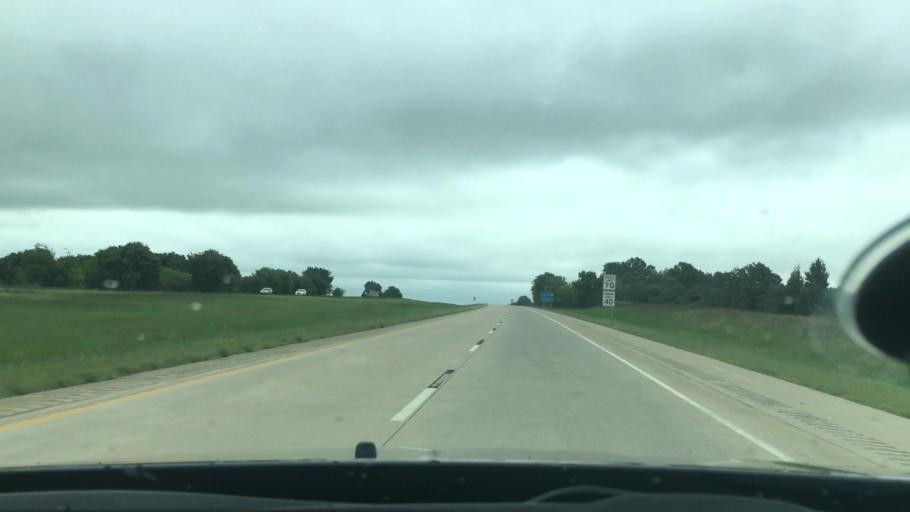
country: US
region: Oklahoma
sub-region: McIntosh County
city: Checotah
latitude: 35.4568
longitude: -95.5818
